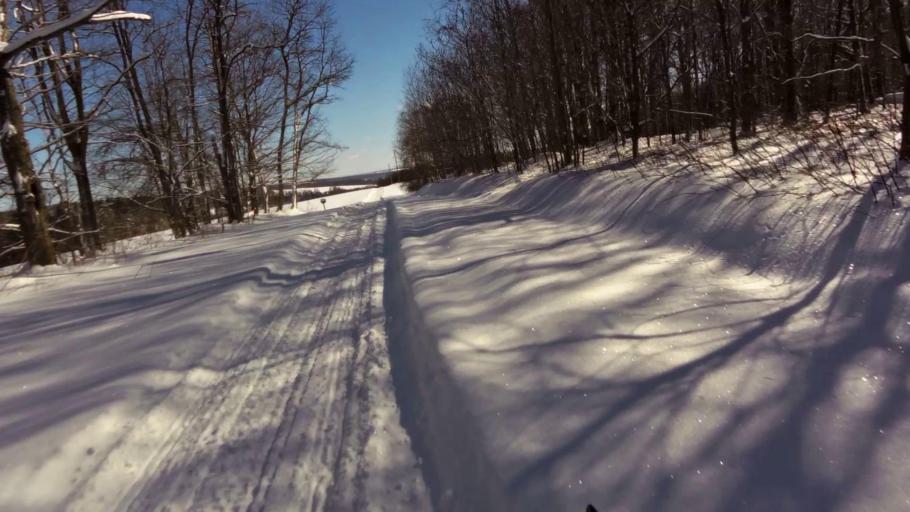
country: US
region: New York
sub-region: Chautauqua County
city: Silver Creek
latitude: 42.3834
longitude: -79.1299
